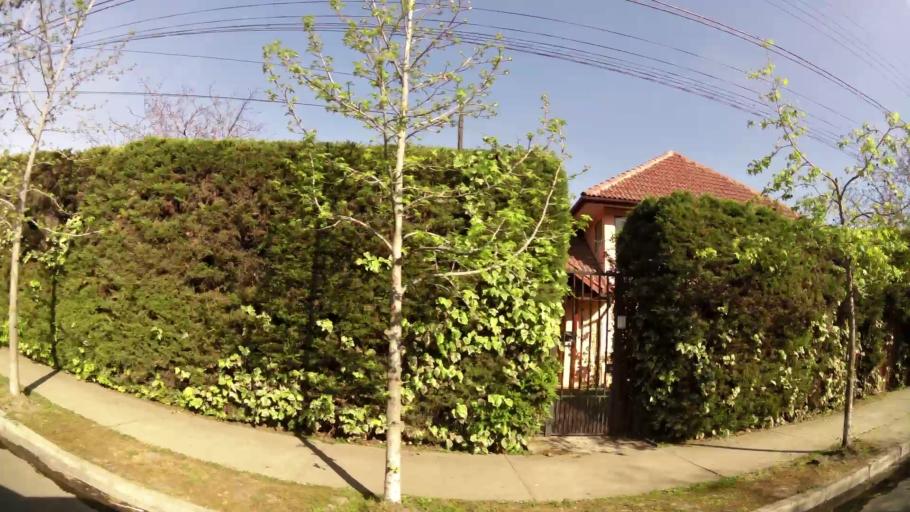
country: CL
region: Santiago Metropolitan
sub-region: Provincia de Santiago
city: Villa Presidente Frei, Nunoa, Santiago, Chile
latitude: -33.4944
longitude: -70.5457
